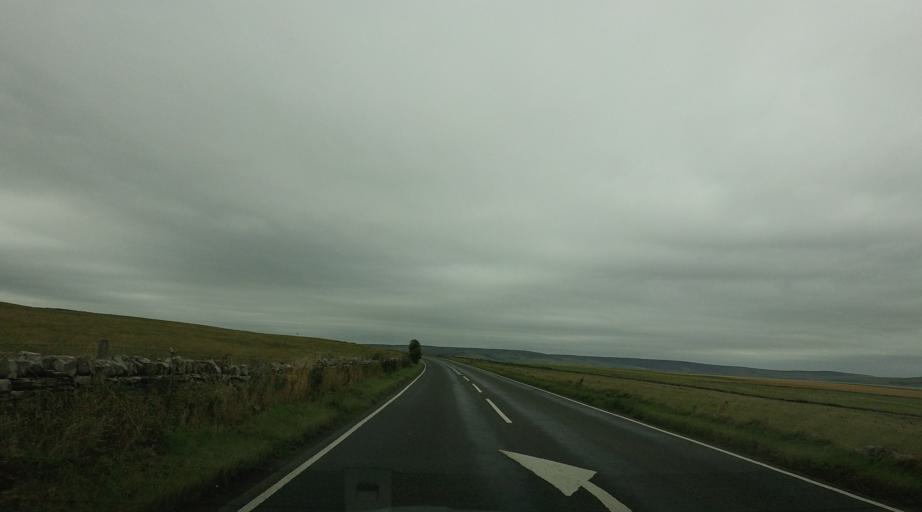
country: GB
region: Scotland
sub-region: Orkney Islands
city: Orkney
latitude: 59.0023
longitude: -3.0002
